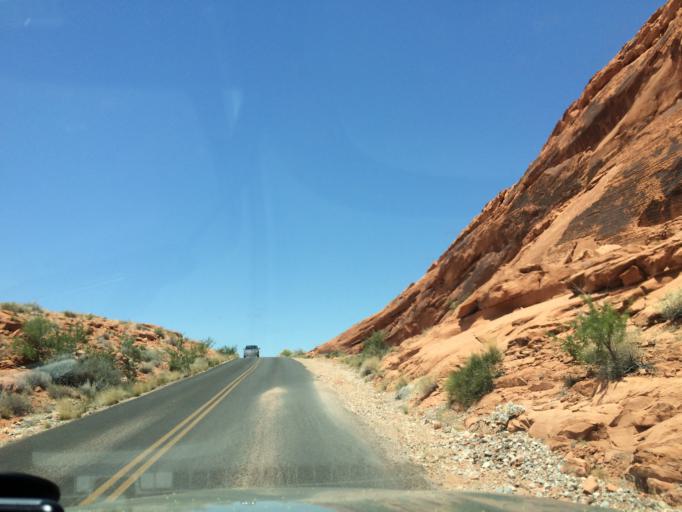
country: US
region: Nevada
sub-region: Clark County
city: Moapa Valley
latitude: 36.4495
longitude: -114.5153
